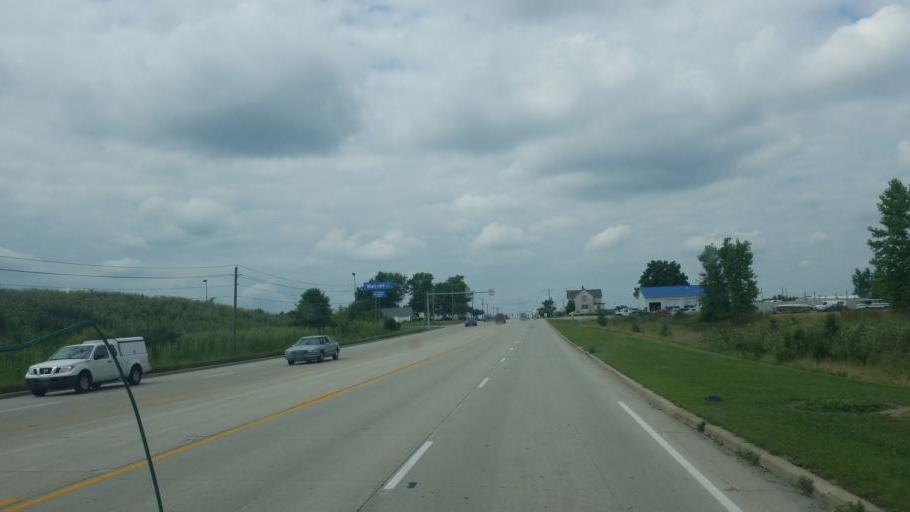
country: US
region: Indiana
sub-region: Adams County
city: Decatur
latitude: 40.8058
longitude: -84.9371
